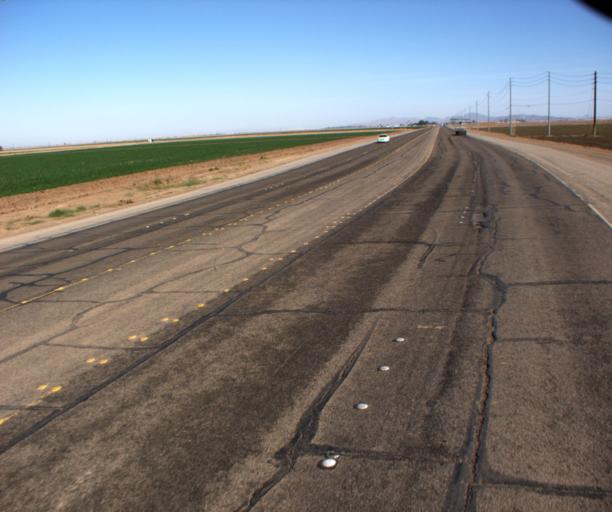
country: US
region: Arizona
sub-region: Yuma County
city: Somerton
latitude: 32.5708
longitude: -114.7698
